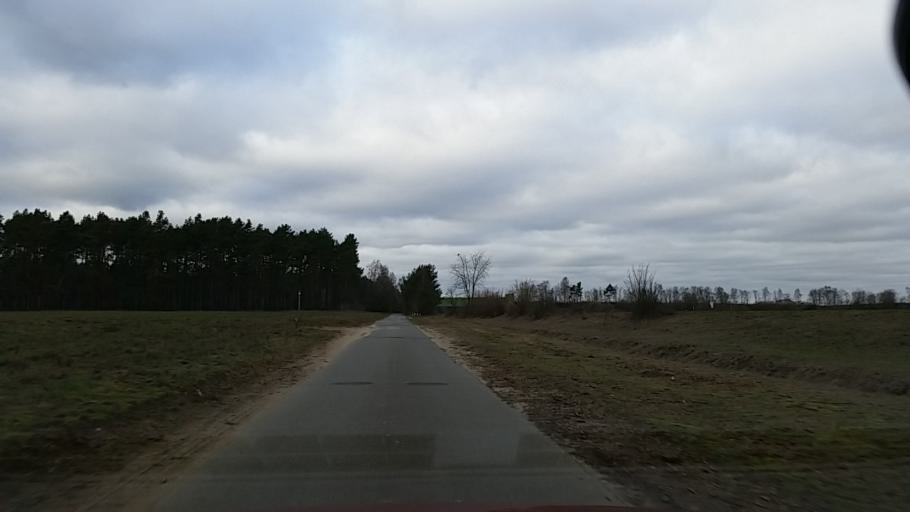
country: DE
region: Lower Saxony
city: Wieren
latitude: 52.8751
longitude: 10.6461
